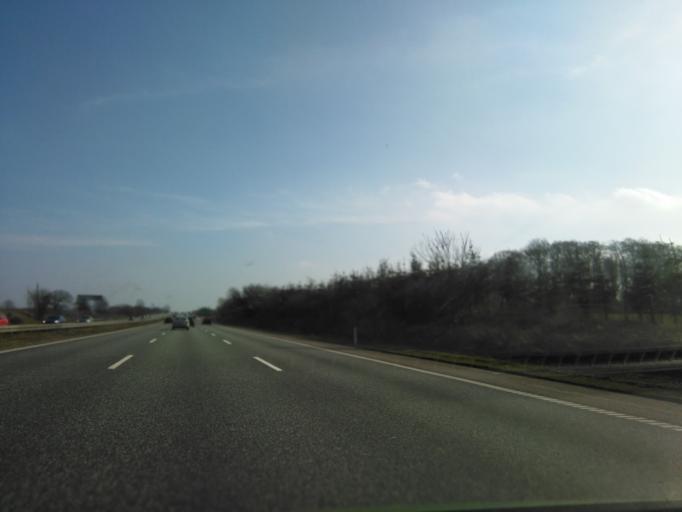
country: DK
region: South Denmark
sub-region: Fredericia Kommune
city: Snoghoj
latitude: 55.5387
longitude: 9.6778
